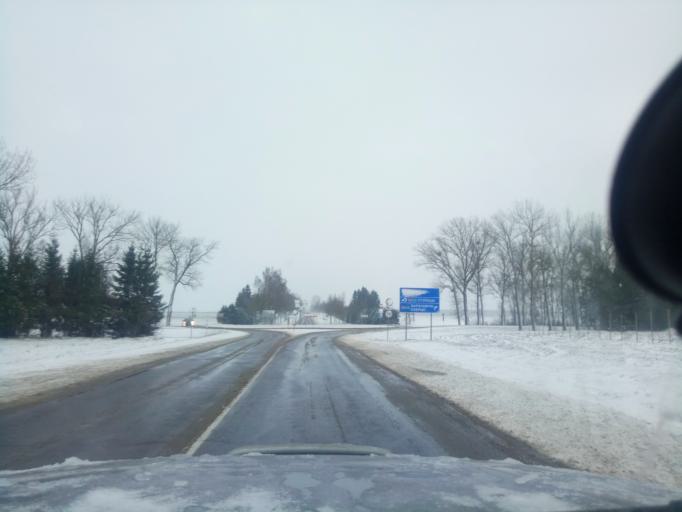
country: BY
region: Minsk
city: Haradzyeya
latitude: 53.3608
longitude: 26.5140
